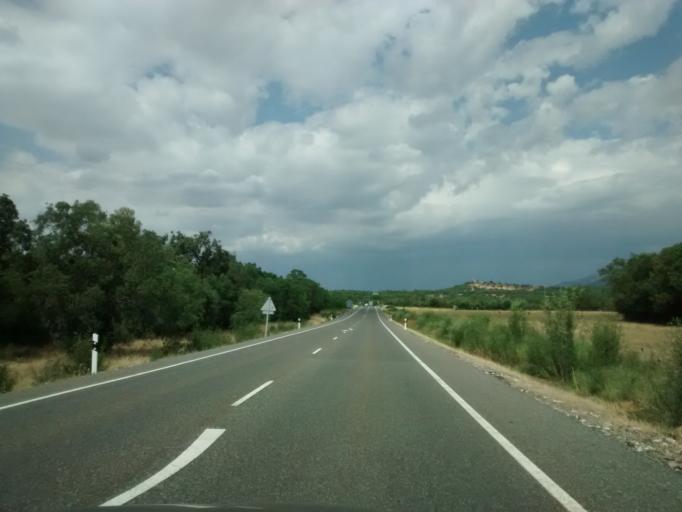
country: ES
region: Castille and Leon
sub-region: Provincia de Segovia
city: Navafria
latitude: 41.0711
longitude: -3.8119
